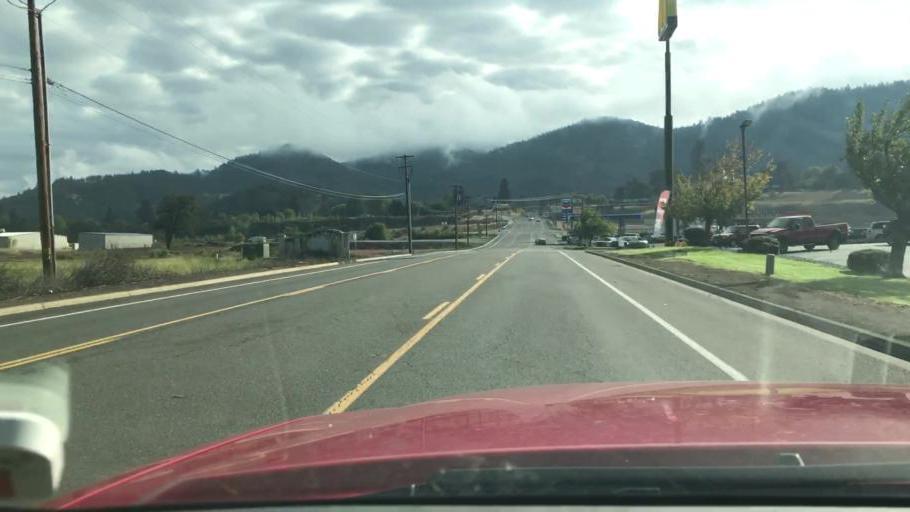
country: US
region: Oregon
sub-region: Douglas County
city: Tri-City
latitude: 42.9733
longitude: -123.3412
